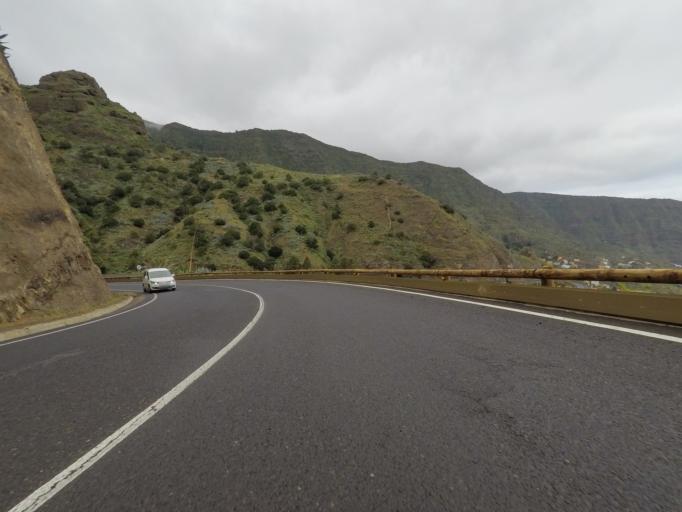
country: ES
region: Canary Islands
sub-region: Provincia de Santa Cruz de Tenerife
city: Hermigua
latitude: 28.1432
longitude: -17.1982
